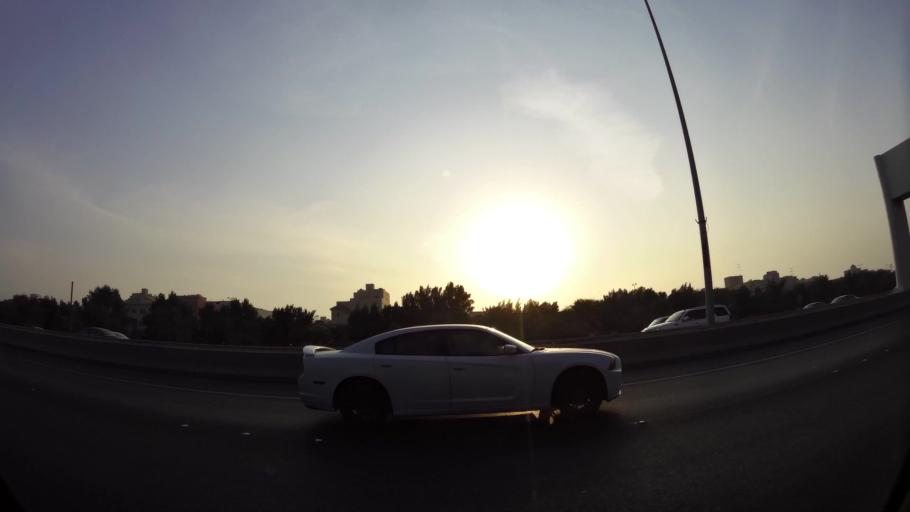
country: KW
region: Muhafazat Hawalli
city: Salwa
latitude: 29.2875
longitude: 48.0737
